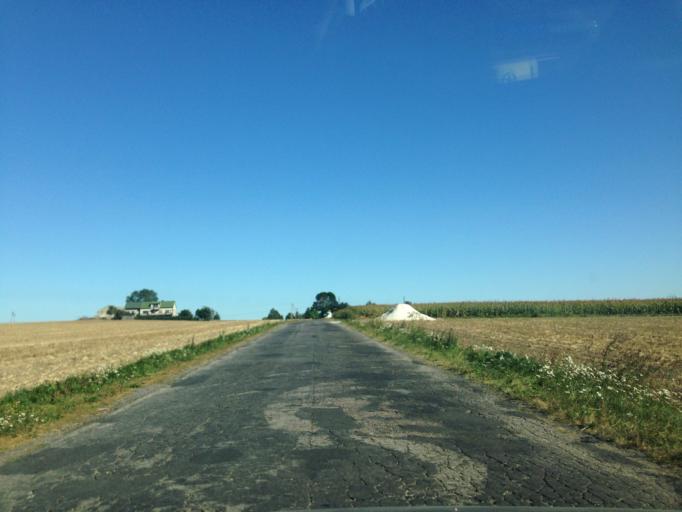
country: PL
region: Kujawsko-Pomorskie
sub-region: Powiat brodnicki
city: Swiedziebnia
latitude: 53.2003
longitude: 19.5530
